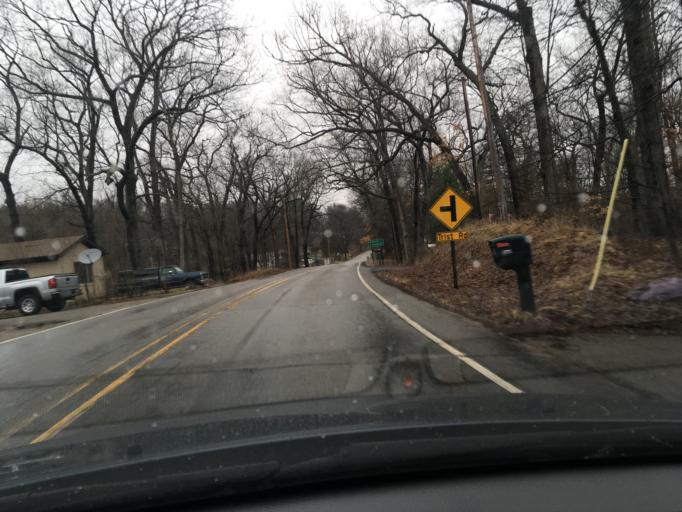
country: US
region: Michigan
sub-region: Jackson County
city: Grass Lake
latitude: 42.3335
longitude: -84.1552
